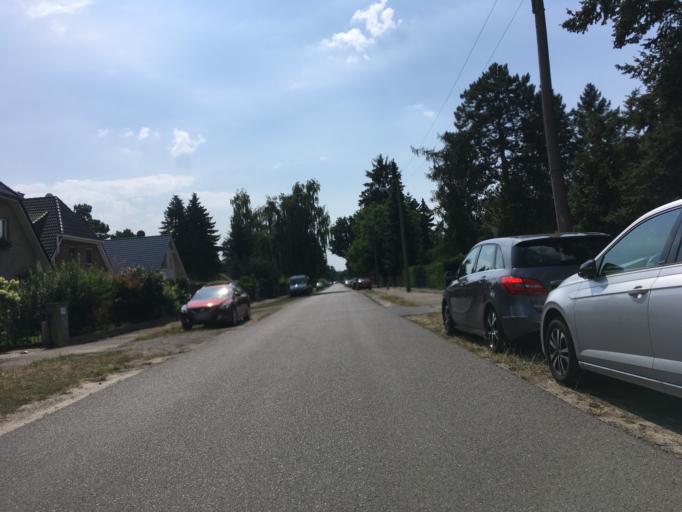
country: DE
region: Berlin
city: Mahlsdorf
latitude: 52.4814
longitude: 13.6105
